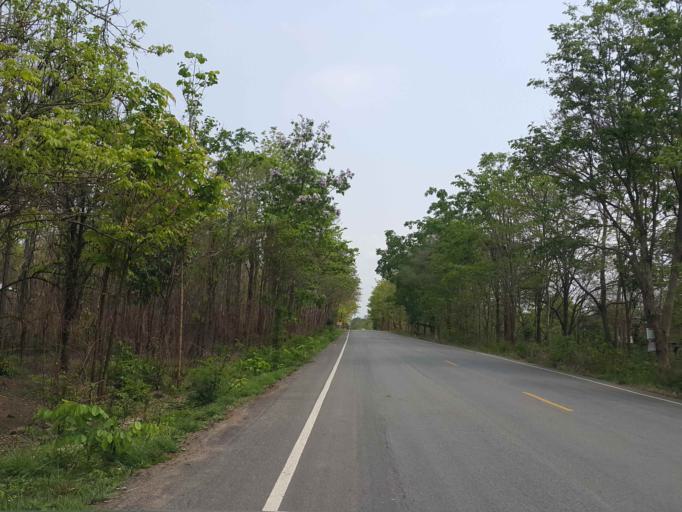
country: TH
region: Sukhothai
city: Thung Saliam
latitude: 17.3817
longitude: 99.3998
